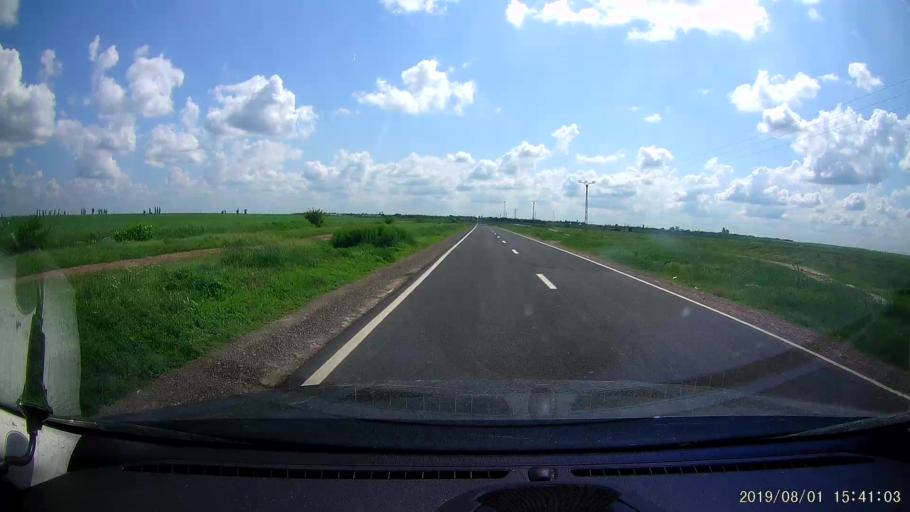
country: RO
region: Braila
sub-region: Comuna Baraganul
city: Baraganul
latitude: 44.8282
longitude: 27.5328
